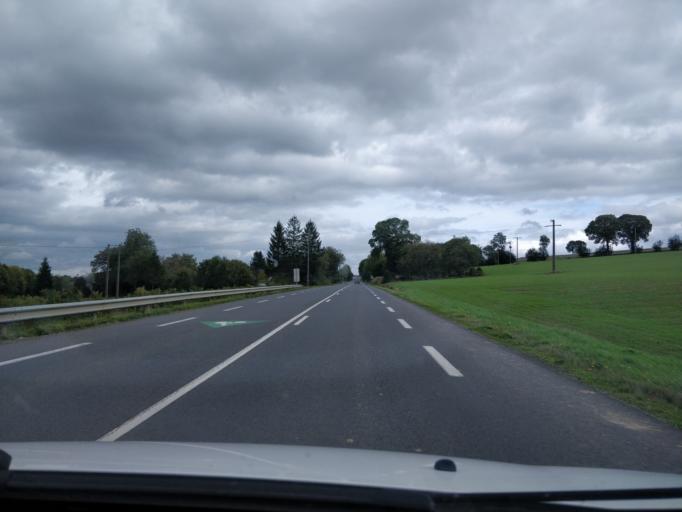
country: FR
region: Lower Normandy
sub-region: Departement du Calvados
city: Vire
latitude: 48.8421
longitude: -0.9367
